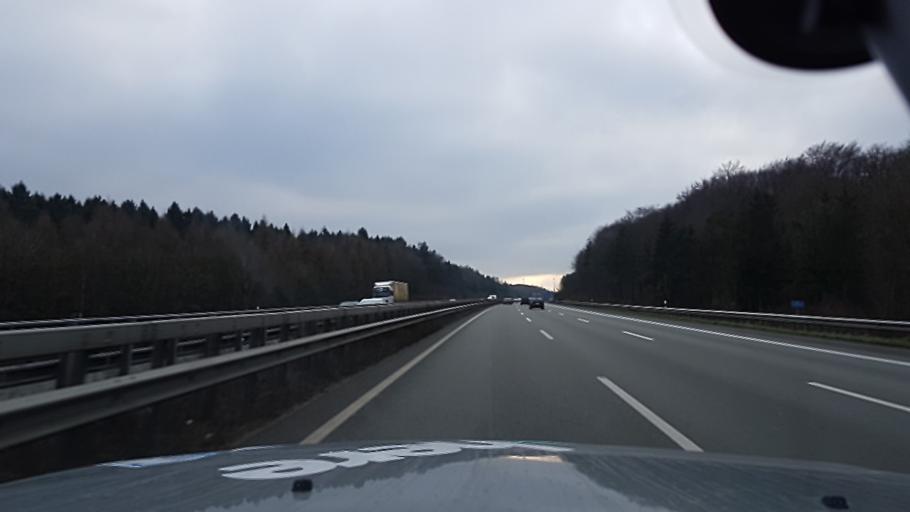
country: DE
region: Lower Saxony
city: Wallenhorst
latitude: 52.3679
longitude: 8.0423
